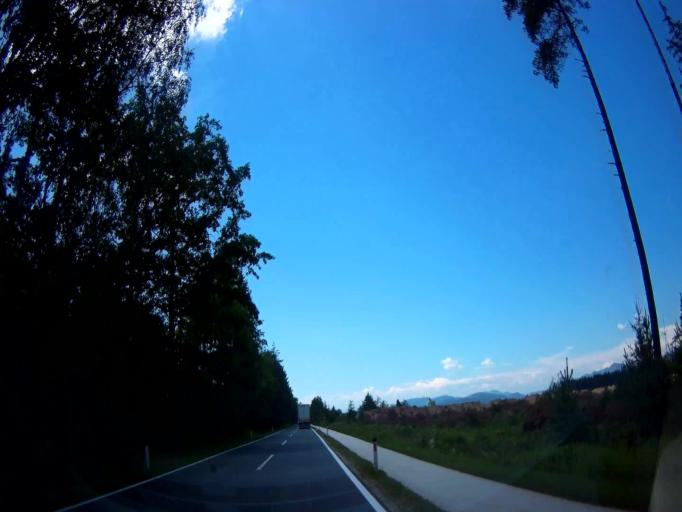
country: AT
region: Carinthia
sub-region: Politischer Bezirk Volkermarkt
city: Globasnitz
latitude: 46.6076
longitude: 14.6935
